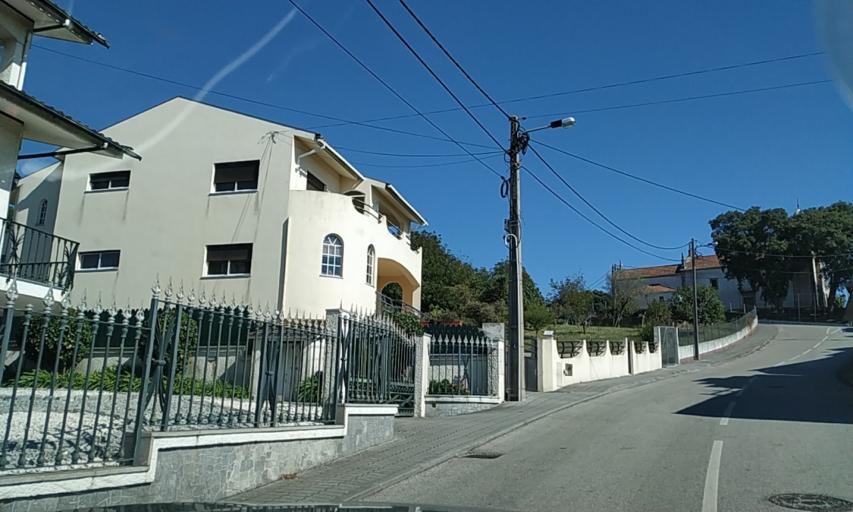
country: PT
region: Aveiro
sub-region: Estarreja
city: Salreu
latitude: 40.7517
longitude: -8.5583
